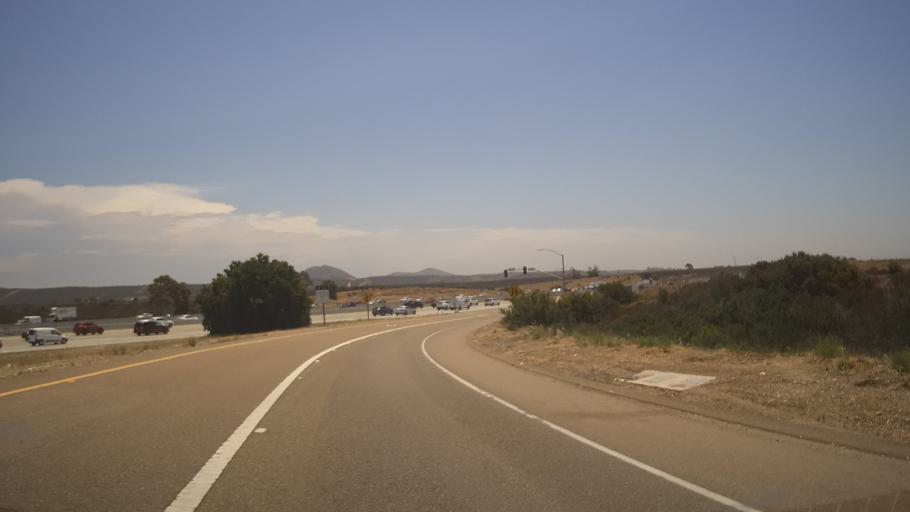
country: US
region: California
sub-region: San Diego County
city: Poway
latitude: 32.8795
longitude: -117.1096
